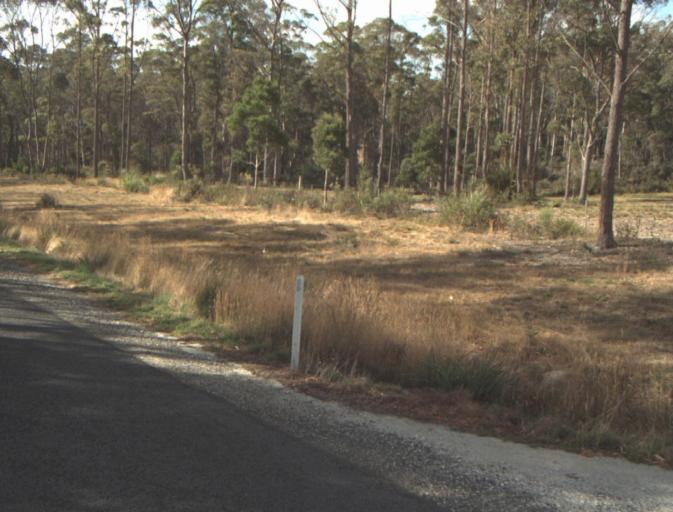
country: AU
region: Tasmania
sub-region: Dorset
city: Bridport
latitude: -41.1151
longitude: 147.2026
